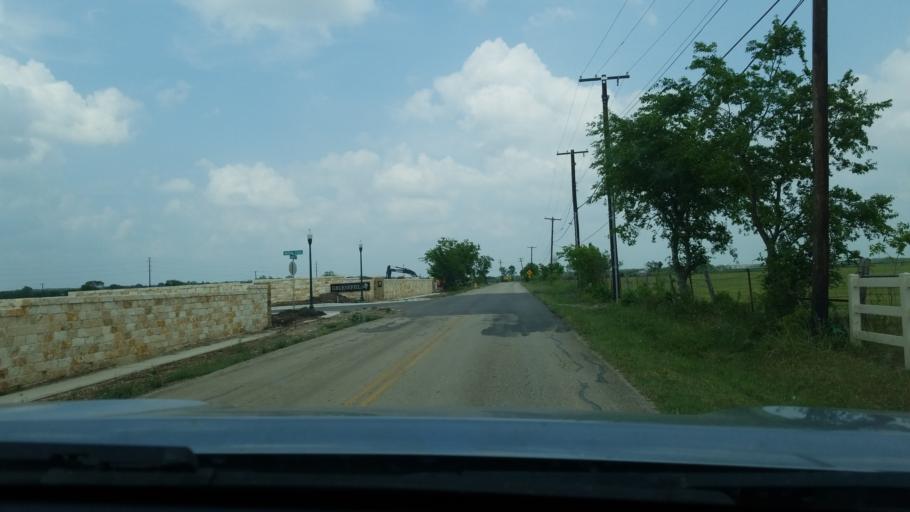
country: US
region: Texas
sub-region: Comal County
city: New Braunfels
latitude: 29.7481
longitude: -98.0929
